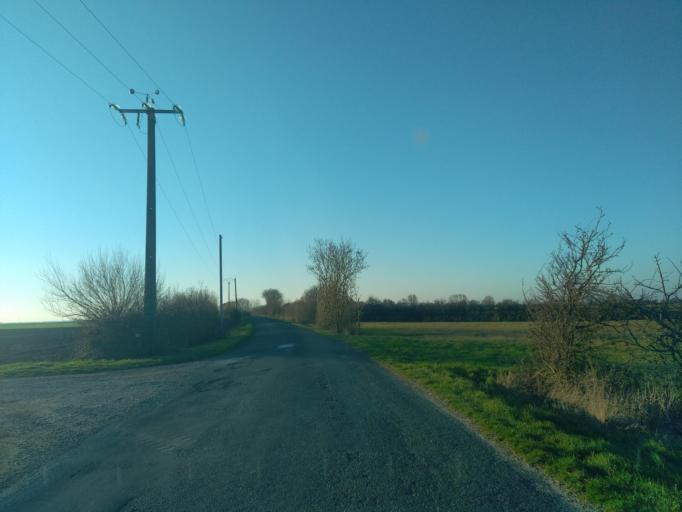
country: FR
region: Pays de la Loire
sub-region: Departement de la Vendee
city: Triaize
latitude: 46.3902
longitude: -1.2792
